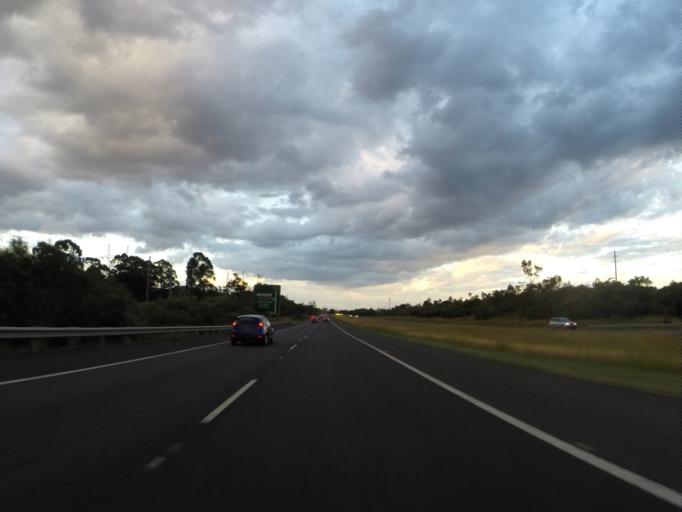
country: AU
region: New South Wales
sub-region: Campbelltown Municipality
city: Glen Alpine
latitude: -34.0811
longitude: 150.7721
